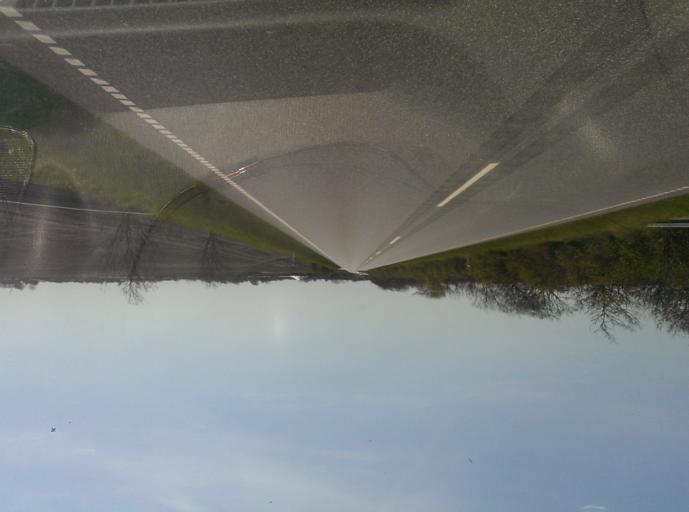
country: DK
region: South Denmark
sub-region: Esbjerg Kommune
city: Bramming
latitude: 55.4294
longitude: 8.6692
